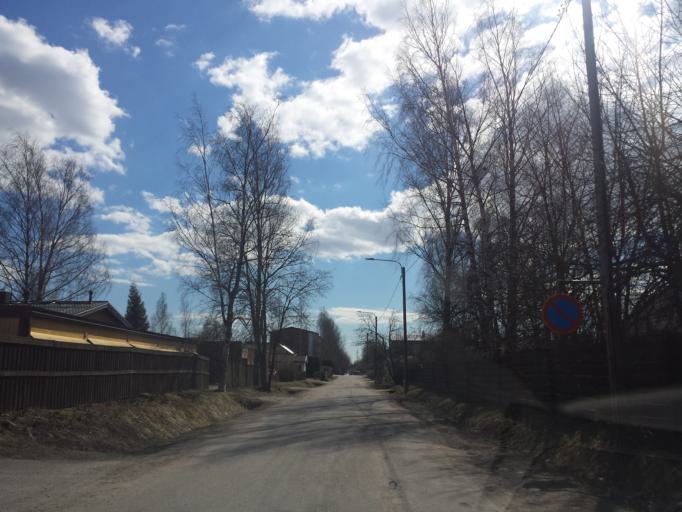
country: FI
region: Uusimaa
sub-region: Helsinki
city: Vantaa
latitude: 60.2962
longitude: 25.0232
